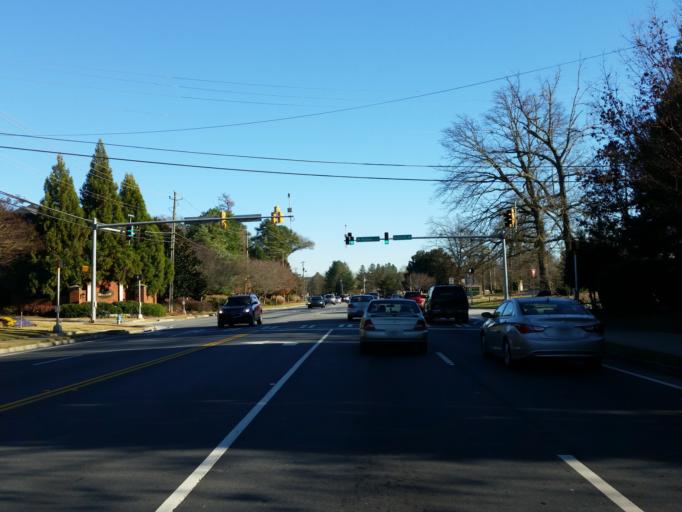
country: US
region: Georgia
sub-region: Cobb County
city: Smyrna
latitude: 33.8779
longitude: -84.5091
